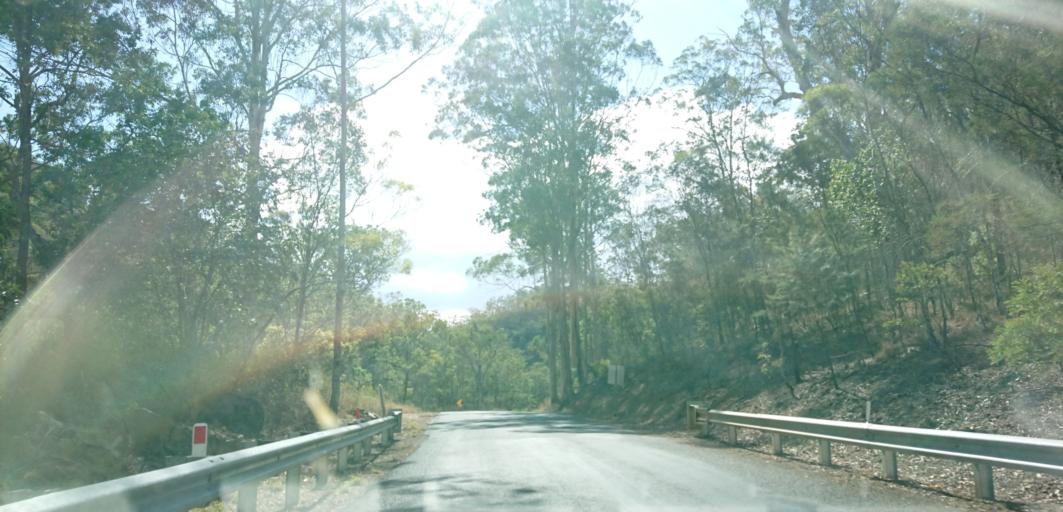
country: AU
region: Queensland
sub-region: Toowoomba
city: Top Camp
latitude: -27.7716
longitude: 152.0896
